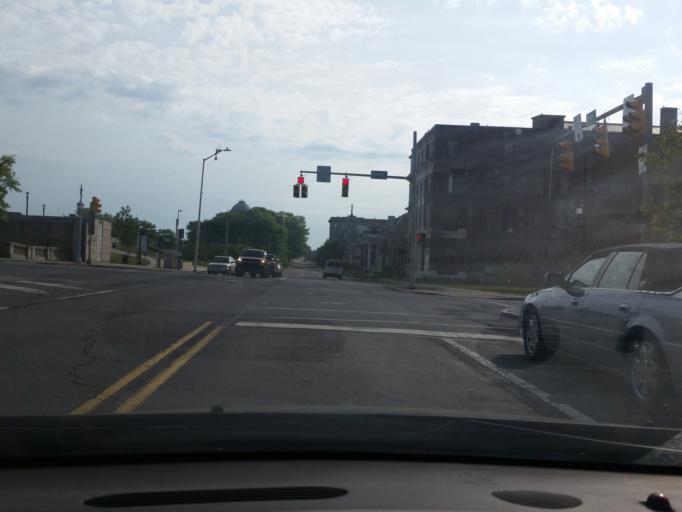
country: US
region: Pennsylvania
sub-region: Luzerne County
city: Wilkes-Barre
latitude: 41.2480
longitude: -75.8843
